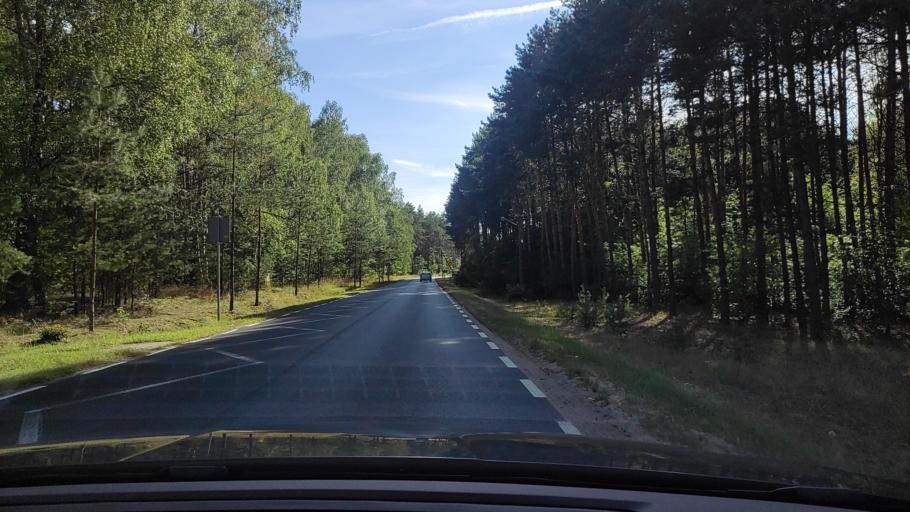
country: PL
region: Greater Poland Voivodeship
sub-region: Powiat poznanski
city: Kobylnica
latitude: 52.5155
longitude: 17.1357
